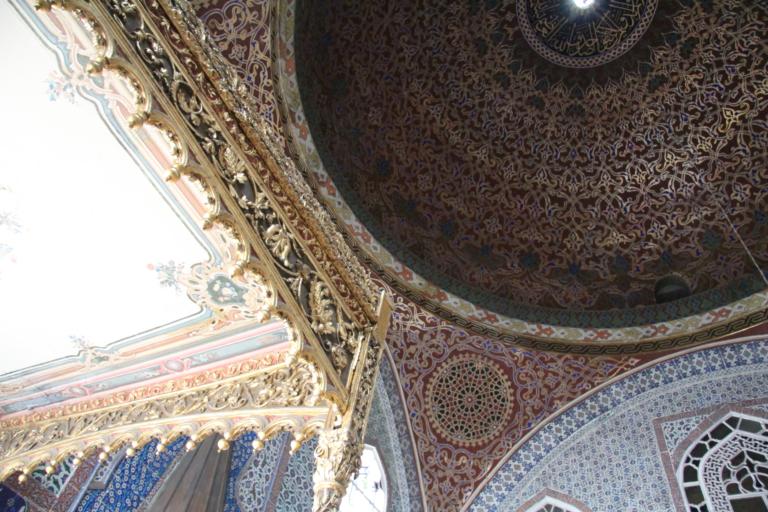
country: TR
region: Istanbul
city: Eminoenue
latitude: 41.0131
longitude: 28.9833
